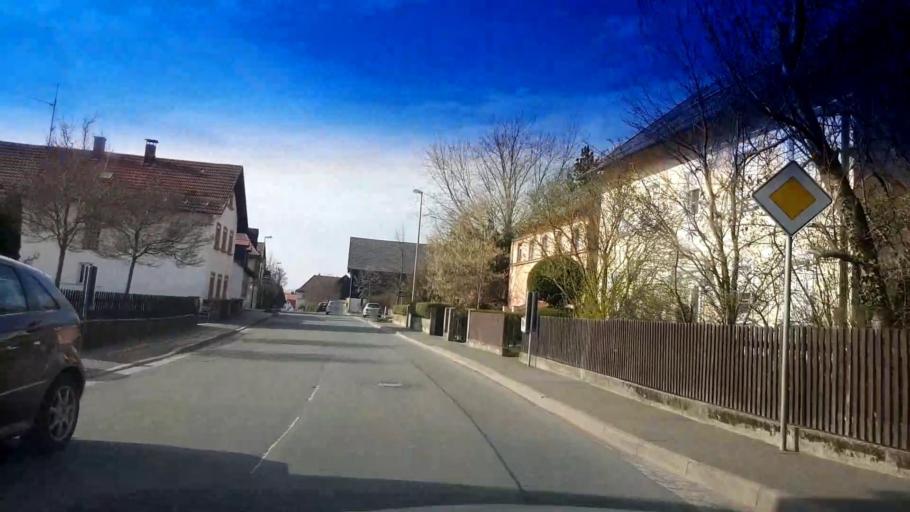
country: DE
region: Bavaria
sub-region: Upper Franconia
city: Harsdorf
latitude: 50.0283
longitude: 11.5677
